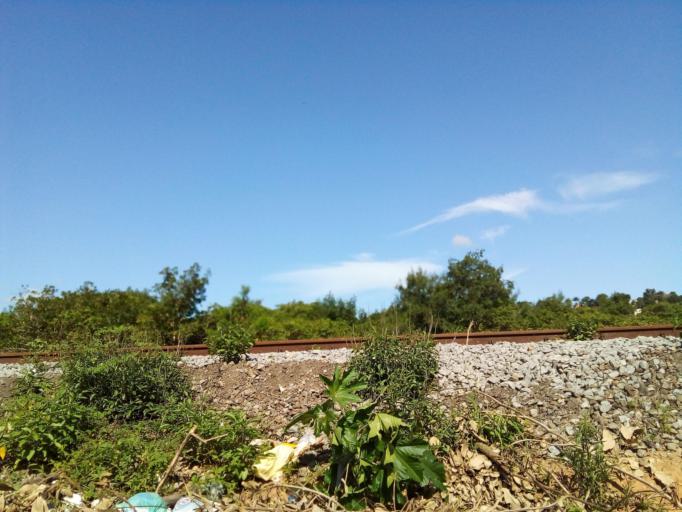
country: BR
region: Espirito Santo
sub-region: Vitoria
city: Vitoria
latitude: -20.2823
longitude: -40.3767
